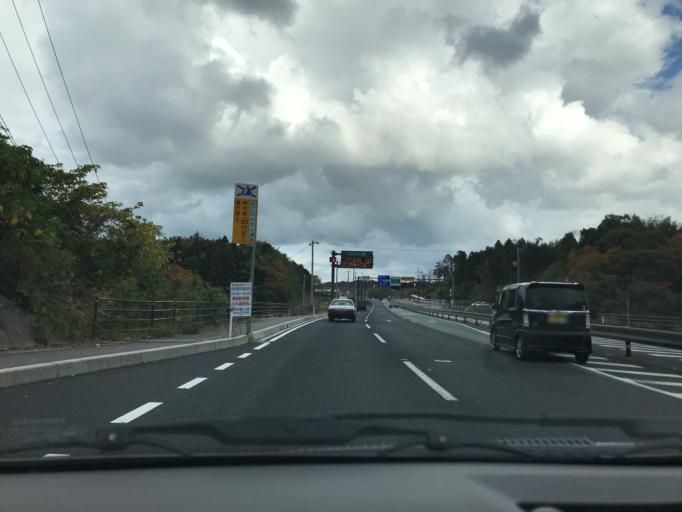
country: JP
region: Shimane
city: Matsue-shi
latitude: 35.4889
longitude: 133.0836
